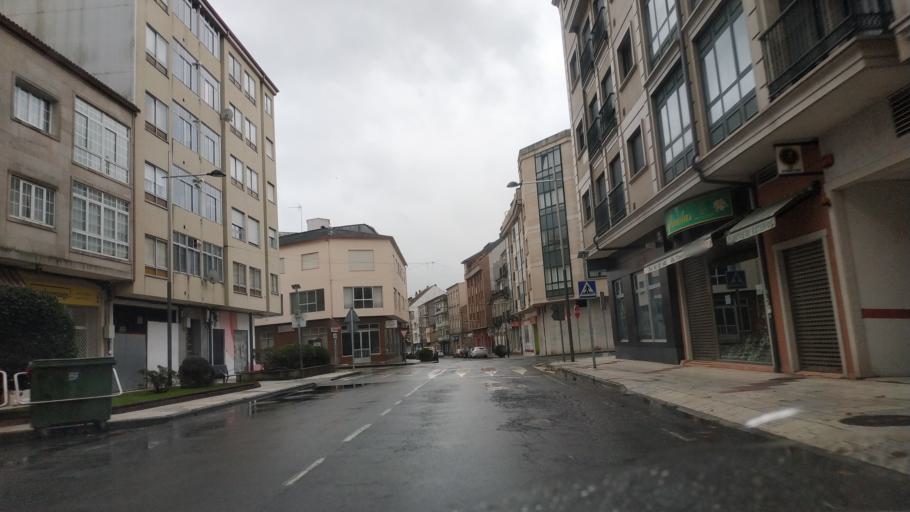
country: ES
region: Galicia
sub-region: Provincia da Coruna
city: Negreira
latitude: 42.9121
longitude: -8.7366
